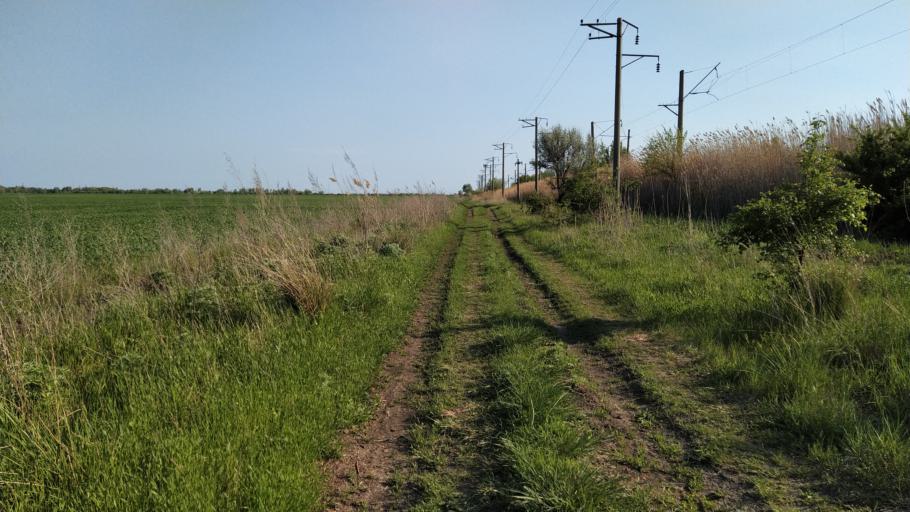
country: RU
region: Rostov
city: Bataysk
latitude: 47.1170
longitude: 39.7138
